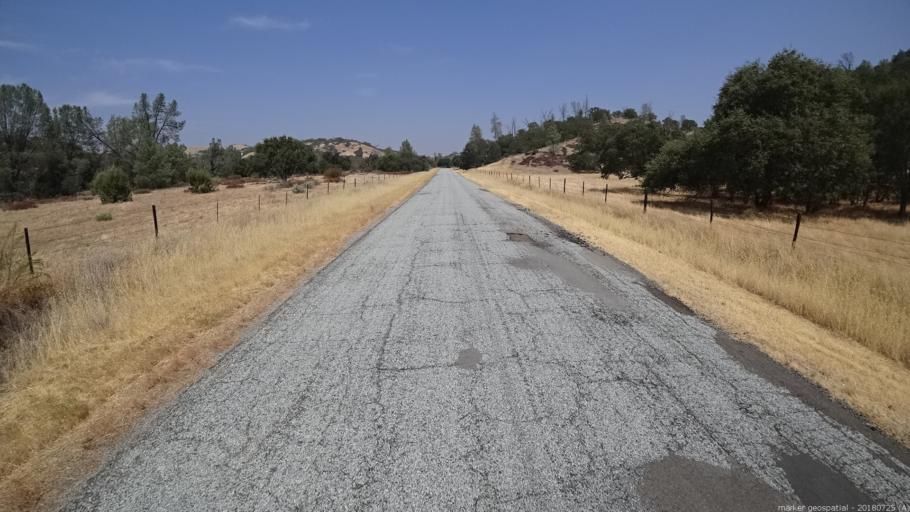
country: US
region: California
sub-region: San Luis Obispo County
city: San Miguel
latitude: 35.8802
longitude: -120.5646
